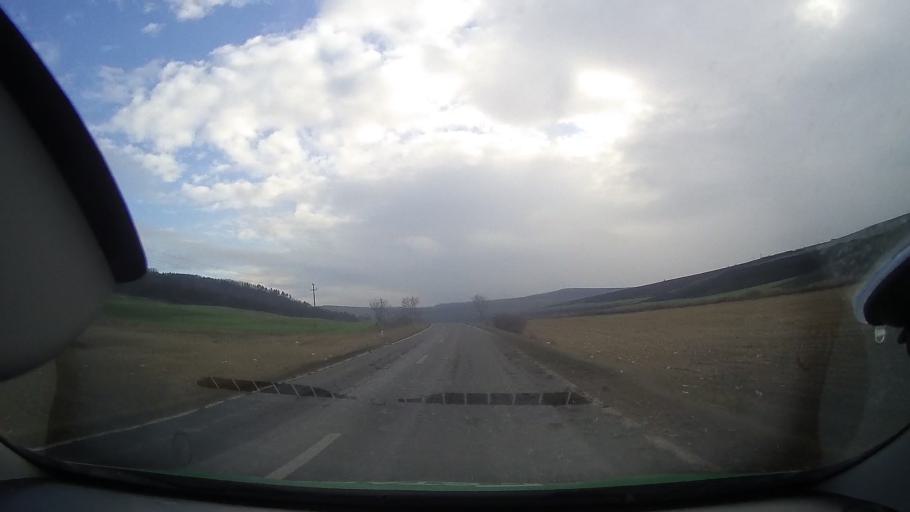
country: RO
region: Mures
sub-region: Comuna Cucerdea
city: Cucerdea
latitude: 46.3743
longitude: 24.2583
